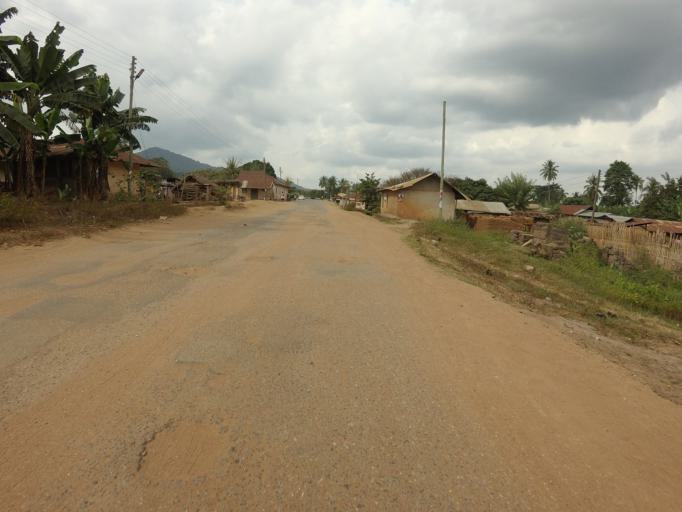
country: GH
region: Volta
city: Ho
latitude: 6.6709
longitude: 0.3536
